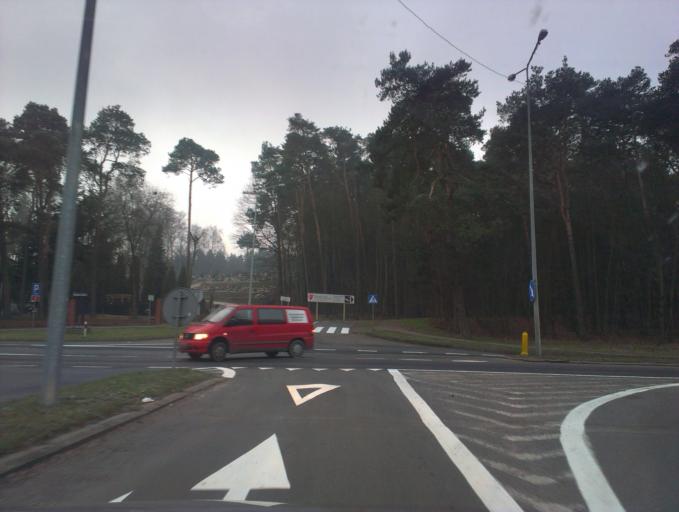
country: PL
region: Greater Poland Voivodeship
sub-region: Powiat chodzieski
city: Chodziez
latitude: 52.9890
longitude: 16.8991
